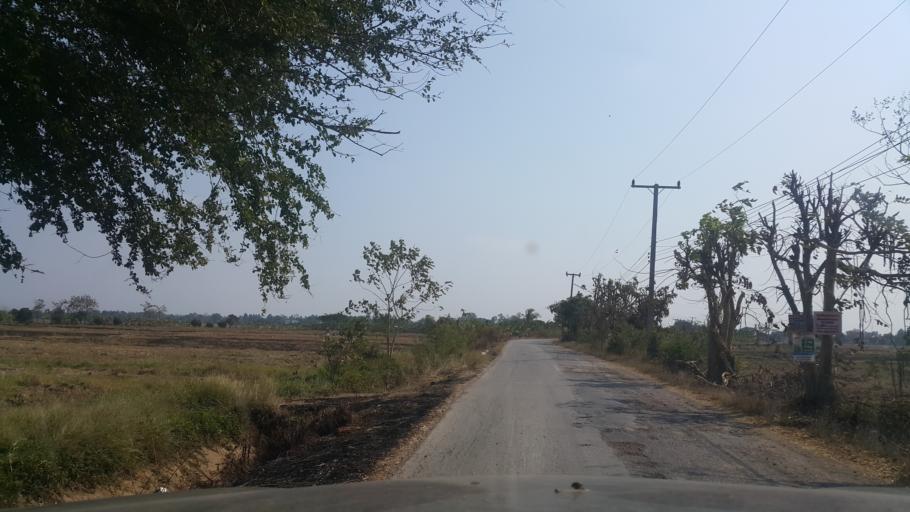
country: TH
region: Nakhon Ratchasima
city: Chok Chai
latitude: 14.6994
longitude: 102.1168
